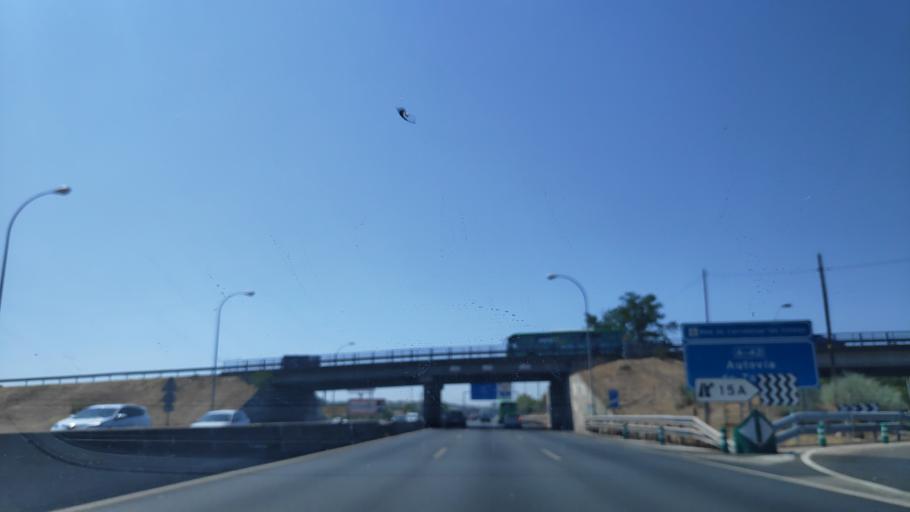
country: ES
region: Madrid
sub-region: Provincia de Madrid
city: Getafe
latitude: 40.2862
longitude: -3.7439
